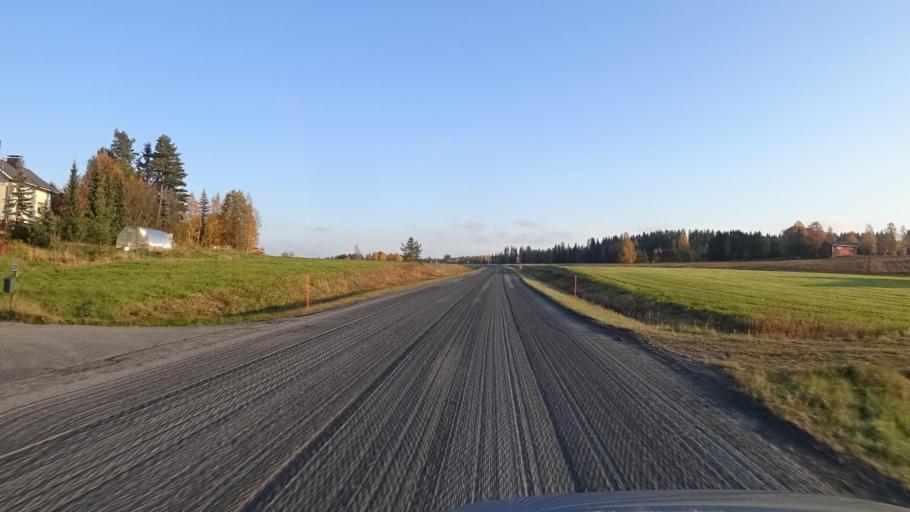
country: FI
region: Haeme
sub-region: Forssa
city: Ypaejae
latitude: 60.7828
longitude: 23.3063
